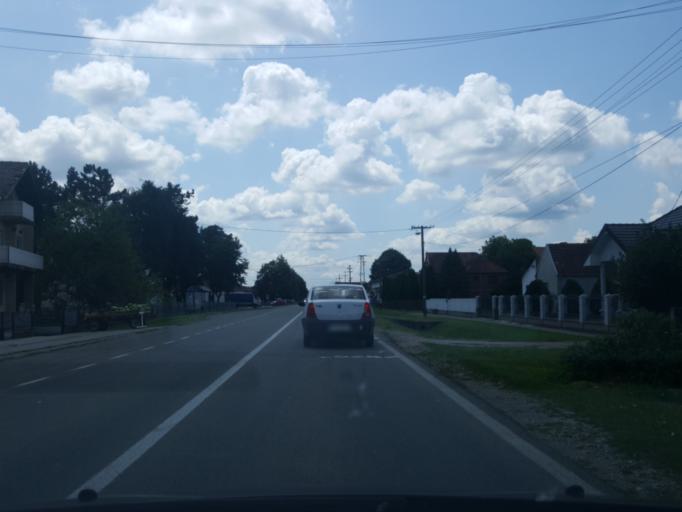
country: RS
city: Ribari
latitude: 44.7282
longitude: 19.4522
